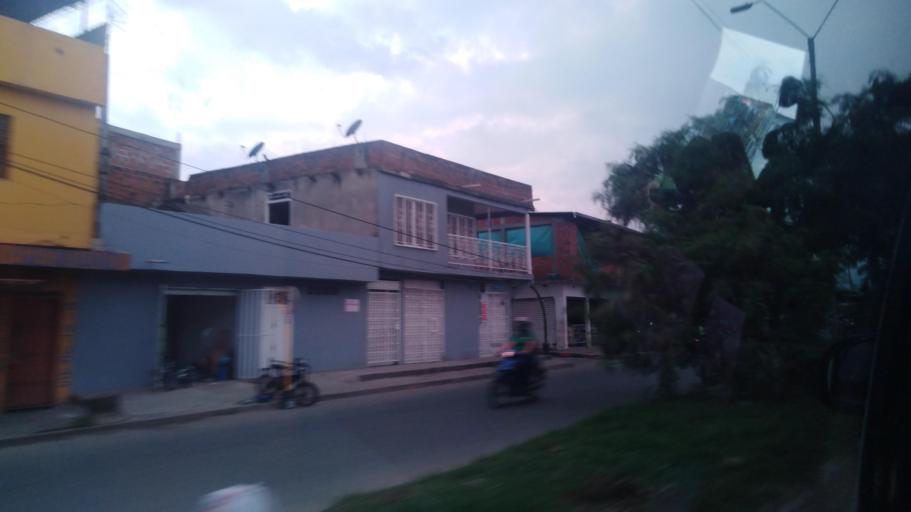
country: CO
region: Valle del Cauca
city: Cali
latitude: 3.4232
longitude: -76.4899
